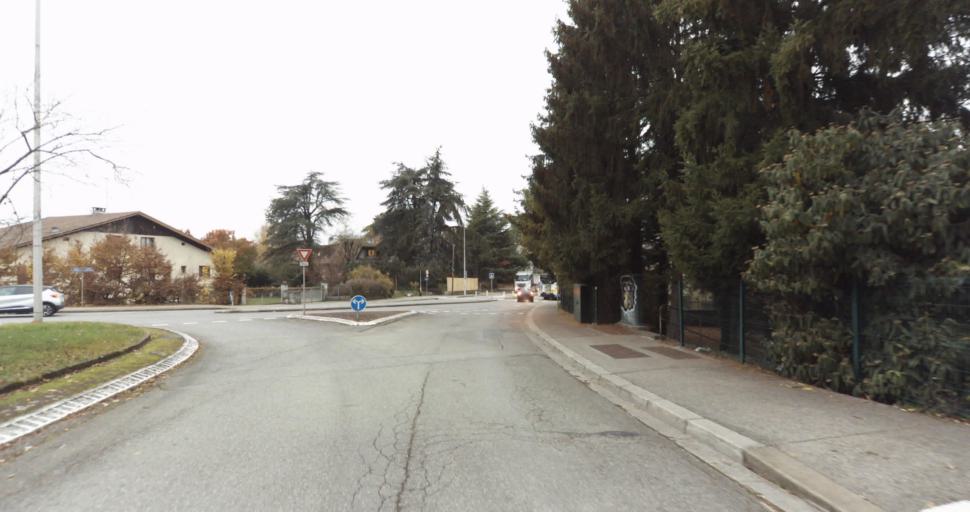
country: FR
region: Rhone-Alpes
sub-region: Departement de la Haute-Savoie
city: Cran-Gevrier
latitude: 45.9026
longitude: 6.1041
